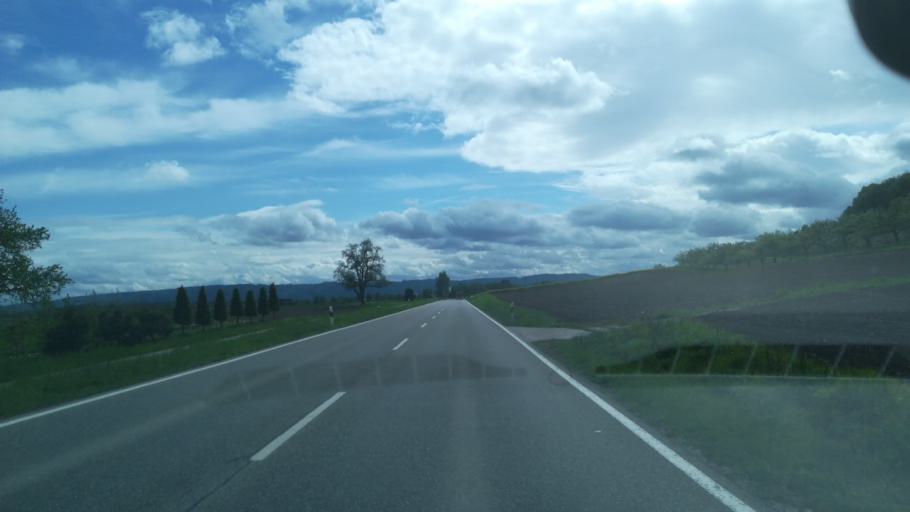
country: DE
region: Baden-Wuerttemberg
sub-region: Freiburg Region
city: Steisslingen
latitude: 47.7911
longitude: 8.9189
